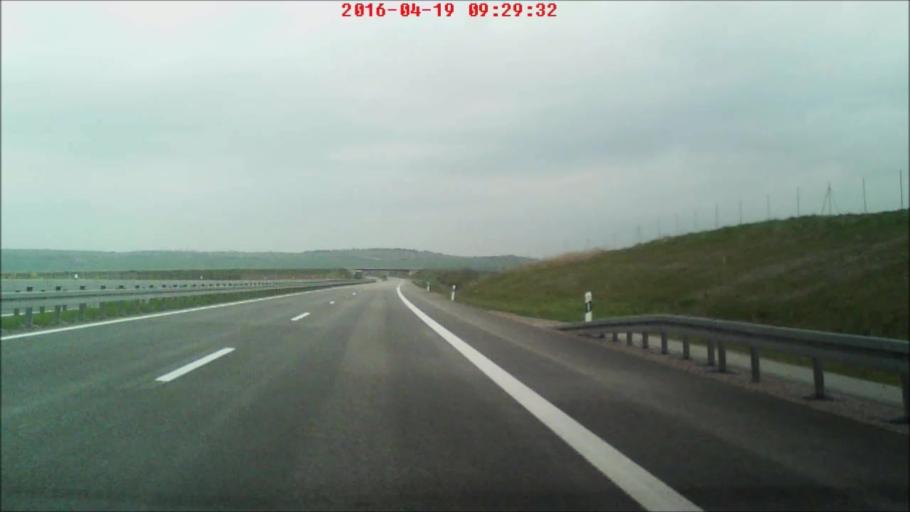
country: DE
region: Thuringia
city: Schillingstedt
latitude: 51.2473
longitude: 11.1903
